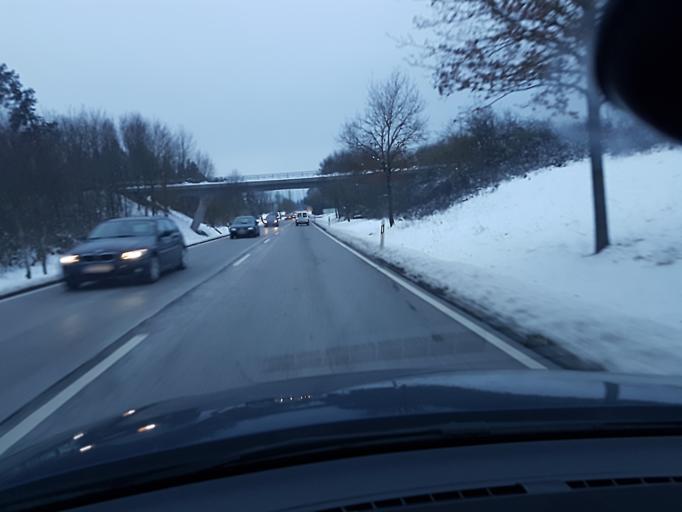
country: DE
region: Baden-Wuerttemberg
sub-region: Freiburg Region
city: Villingen-Schwenningen
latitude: 48.0724
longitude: 8.4844
